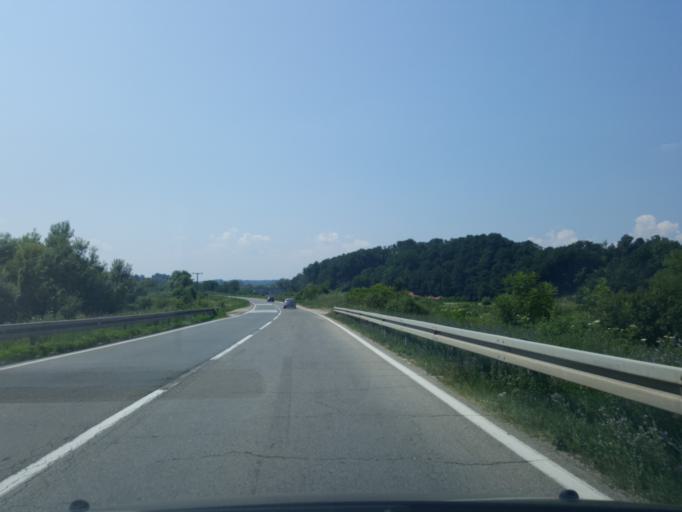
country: RS
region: Central Serbia
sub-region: Belgrade
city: Mladenovac
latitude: 44.5016
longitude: 20.6559
